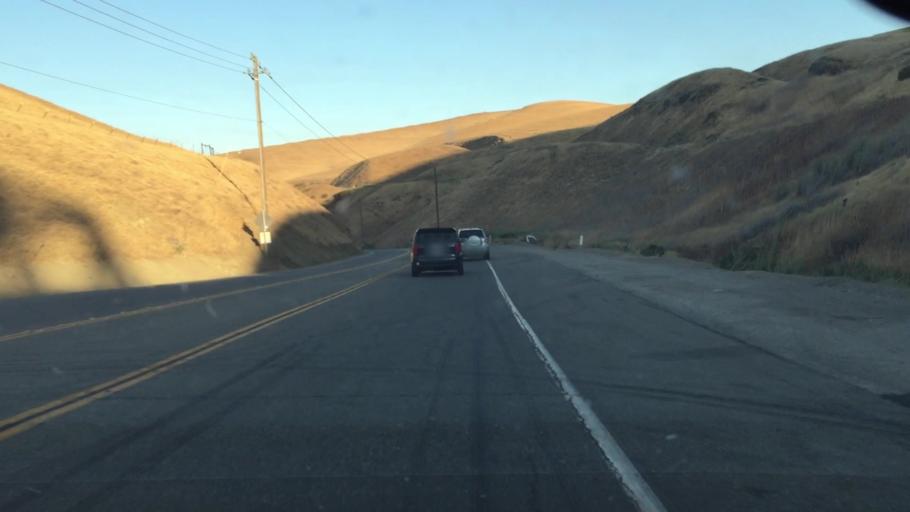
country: US
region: California
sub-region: San Joaquin County
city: Mountain House
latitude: 37.7461
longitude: -121.6538
